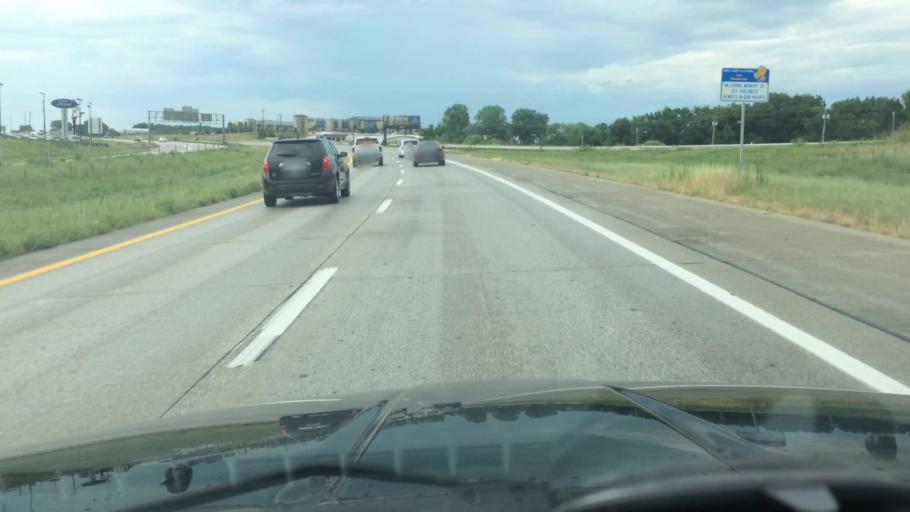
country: US
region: Missouri
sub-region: Cass County
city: Harrisonville
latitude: 38.6619
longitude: -94.3703
